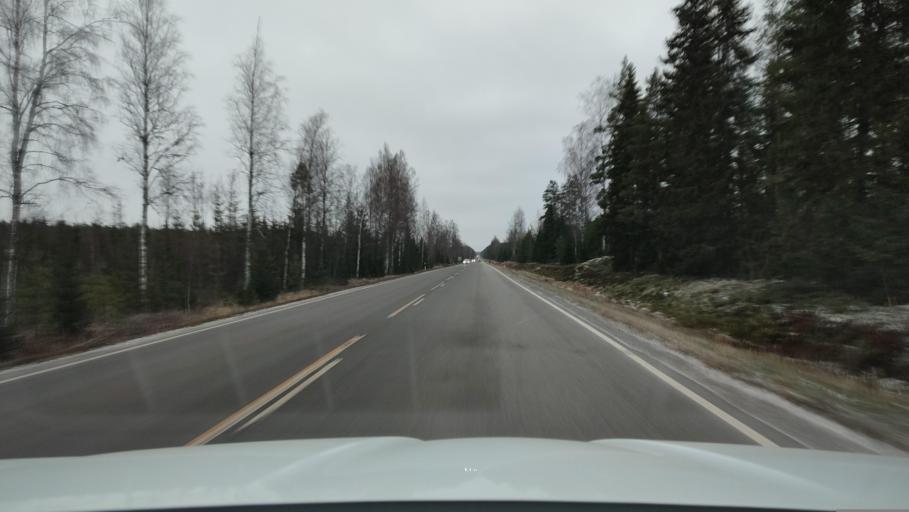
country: FI
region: Ostrobothnia
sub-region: Sydosterbotten
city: Naerpes
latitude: 62.5071
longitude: 21.4516
